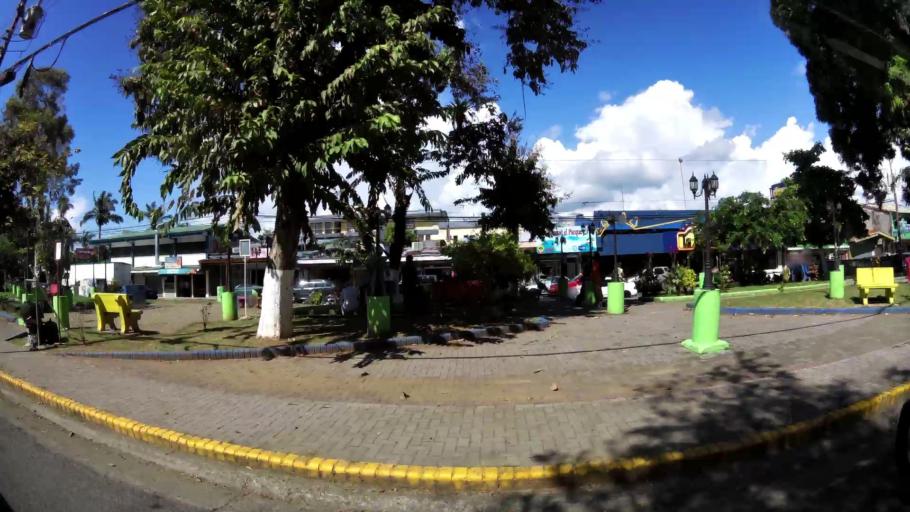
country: CR
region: Puntarenas
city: Quepos
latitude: 9.4298
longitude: -84.1648
